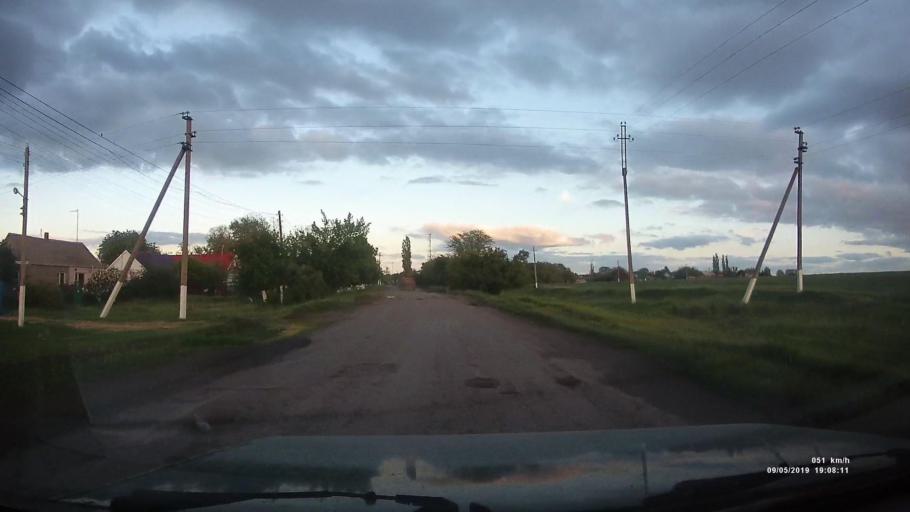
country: RU
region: Krasnodarskiy
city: Kanelovskaya
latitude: 46.7307
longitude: 39.2018
